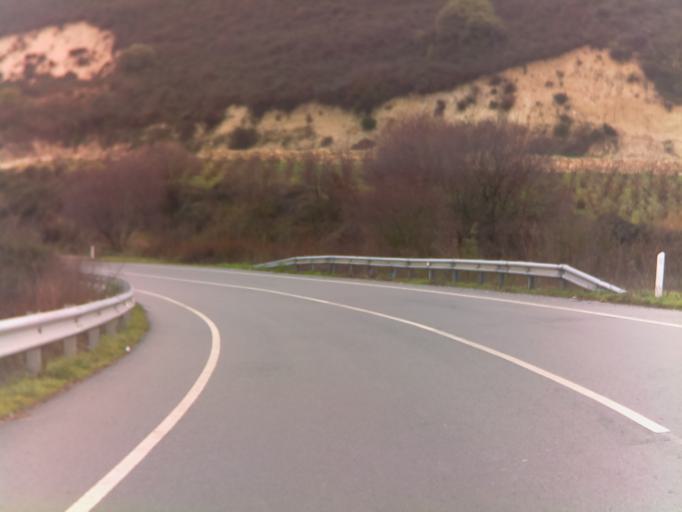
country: CY
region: Pafos
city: Tala
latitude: 34.8998
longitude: 32.4471
